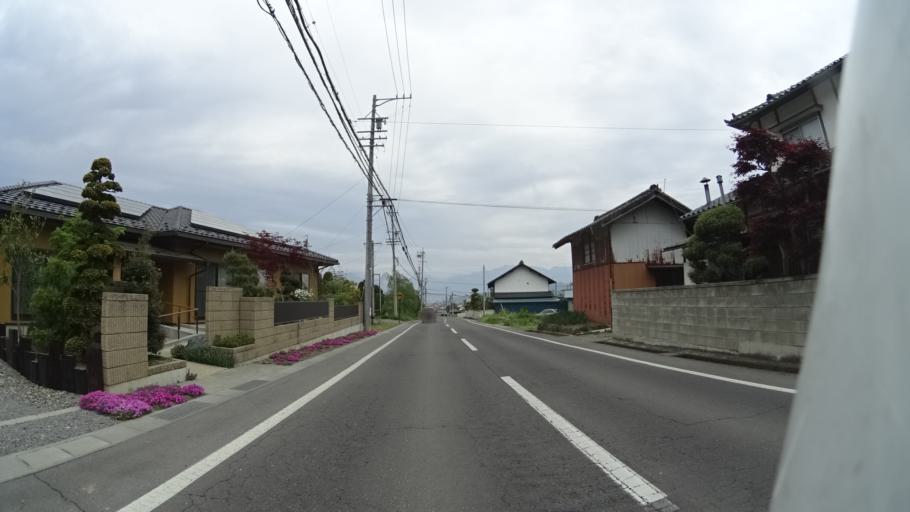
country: JP
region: Nagano
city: Kamimaruko
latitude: 36.3575
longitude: 138.1697
